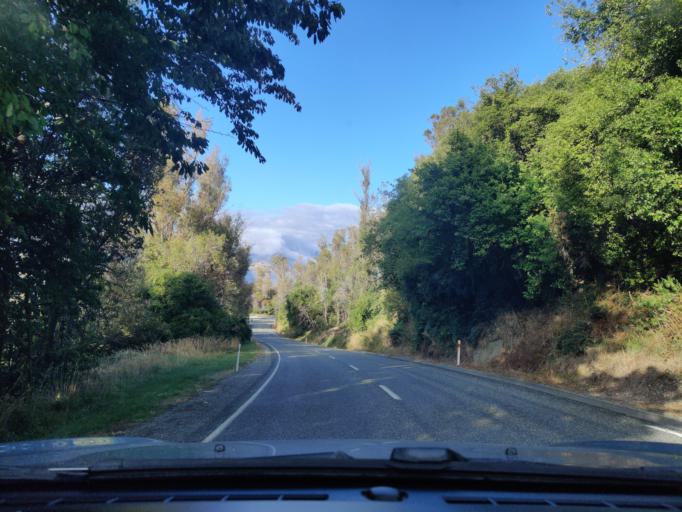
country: NZ
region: Otago
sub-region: Queenstown-Lakes District
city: Queenstown
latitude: -45.0428
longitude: 168.6346
